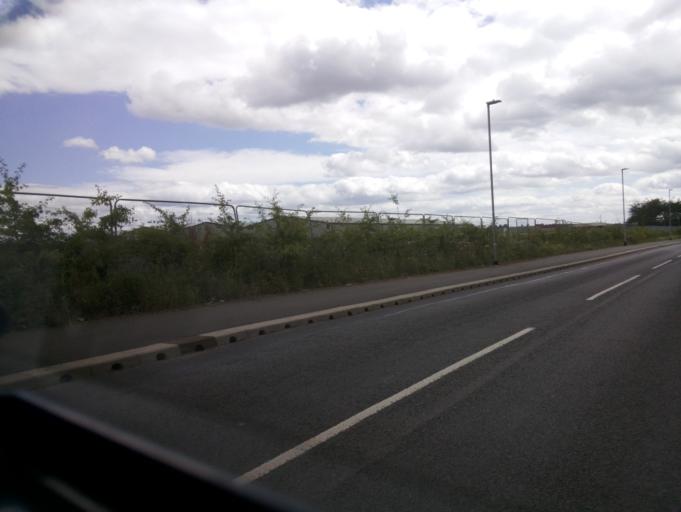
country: GB
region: England
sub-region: Nottinghamshire
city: West Bridgford
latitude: 52.9180
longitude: -1.0865
